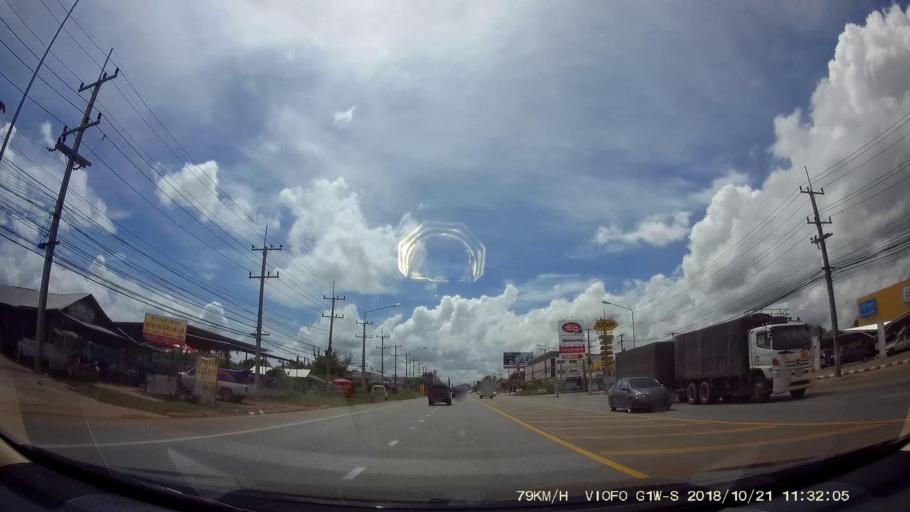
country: TH
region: Chaiyaphum
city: Chaiyaphum
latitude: 15.7627
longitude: 102.0248
